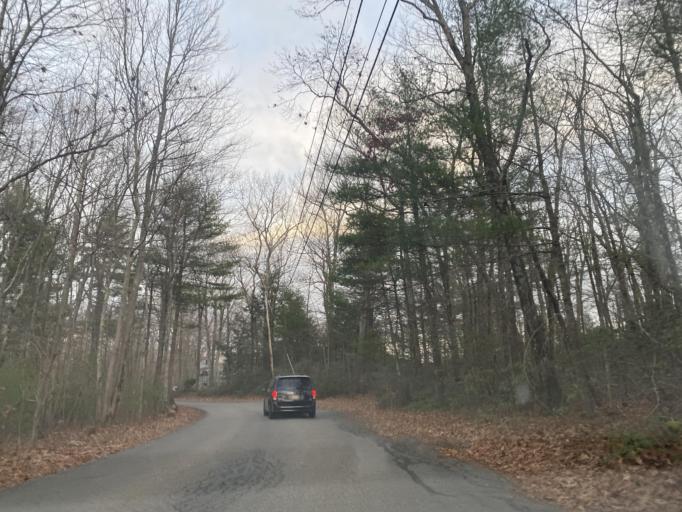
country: US
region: Massachusetts
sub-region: Worcester County
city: Leicester
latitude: 42.2716
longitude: -71.9362
